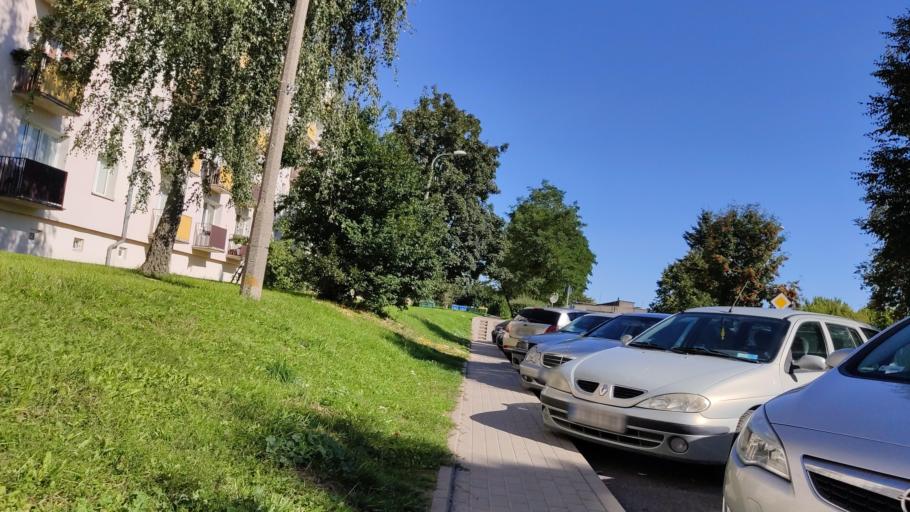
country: PL
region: Kujawsko-Pomorskie
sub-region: Powiat zninski
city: Barcin
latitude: 52.8532
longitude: 17.9422
